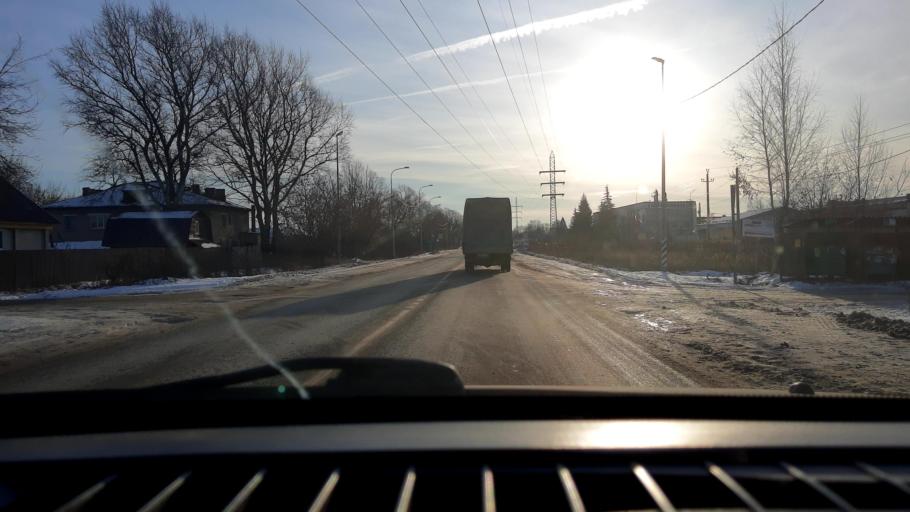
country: RU
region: Nizjnij Novgorod
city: Bor
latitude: 56.3712
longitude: 44.0655
